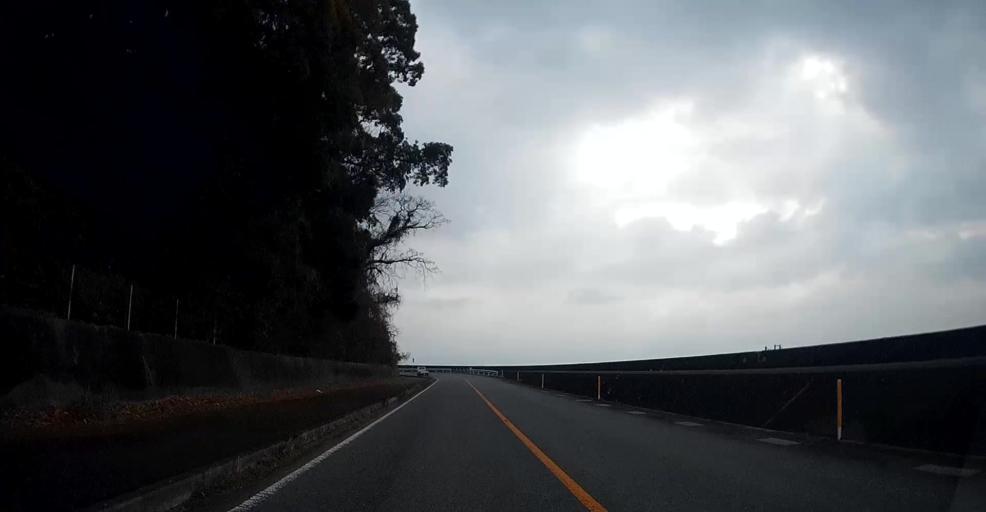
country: JP
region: Kumamoto
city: Matsubase
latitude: 32.6329
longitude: 130.6260
